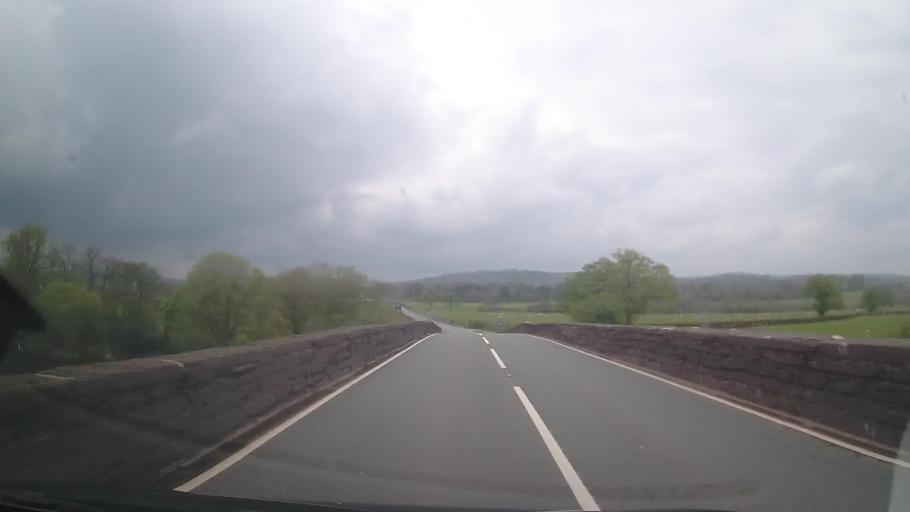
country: GB
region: Wales
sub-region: Denbighshire
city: Corwen
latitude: 52.9785
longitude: -3.3864
